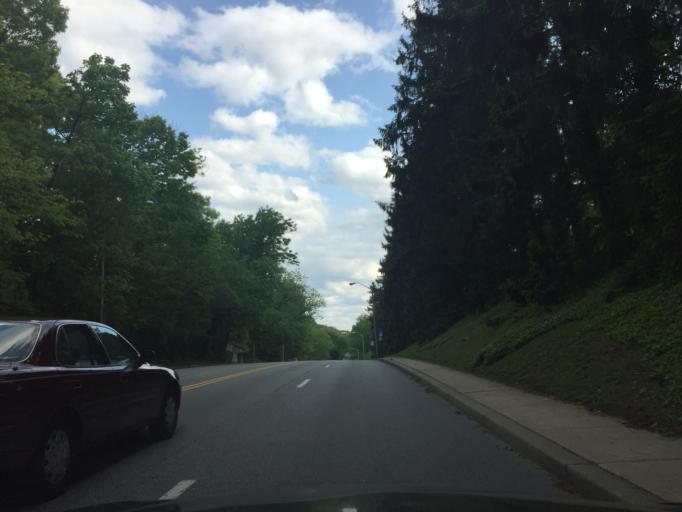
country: US
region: Maryland
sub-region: Baltimore County
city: Towson
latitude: 39.3595
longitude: -76.6457
